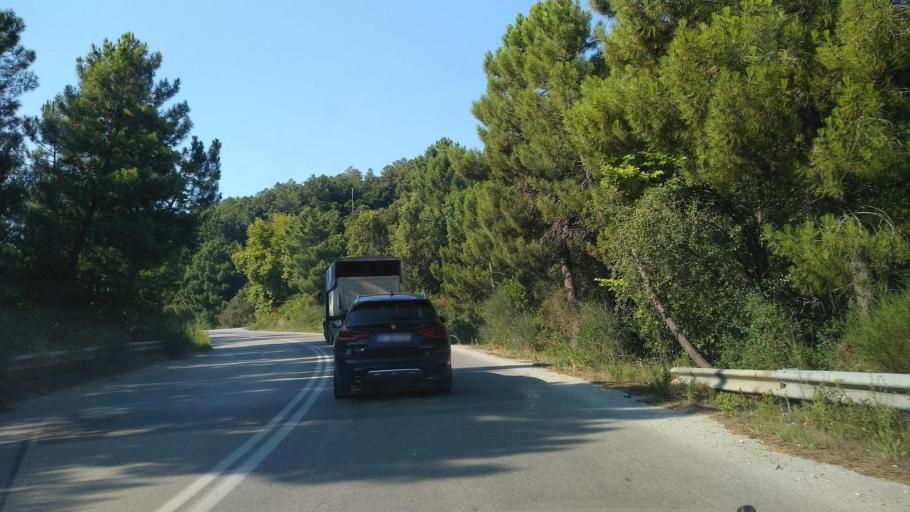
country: GR
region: Central Macedonia
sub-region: Nomos Chalkidikis
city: Stratonion
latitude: 40.5182
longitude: 23.8040
